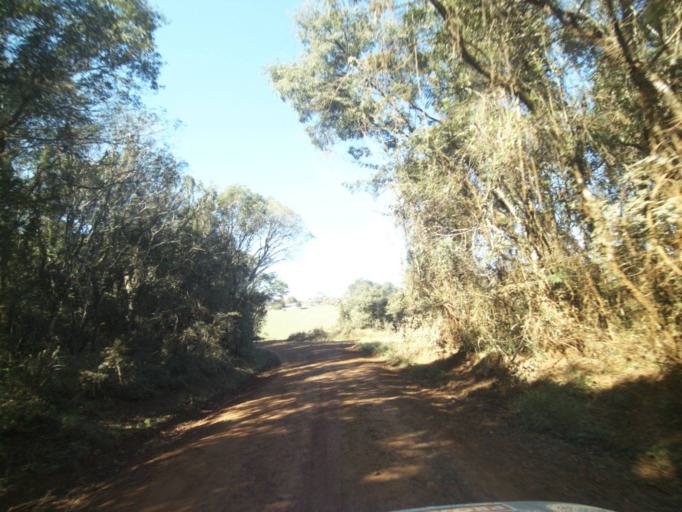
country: BR
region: Parana
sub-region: Tibagi
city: Tibagi
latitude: -24.5795
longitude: -50.6179
